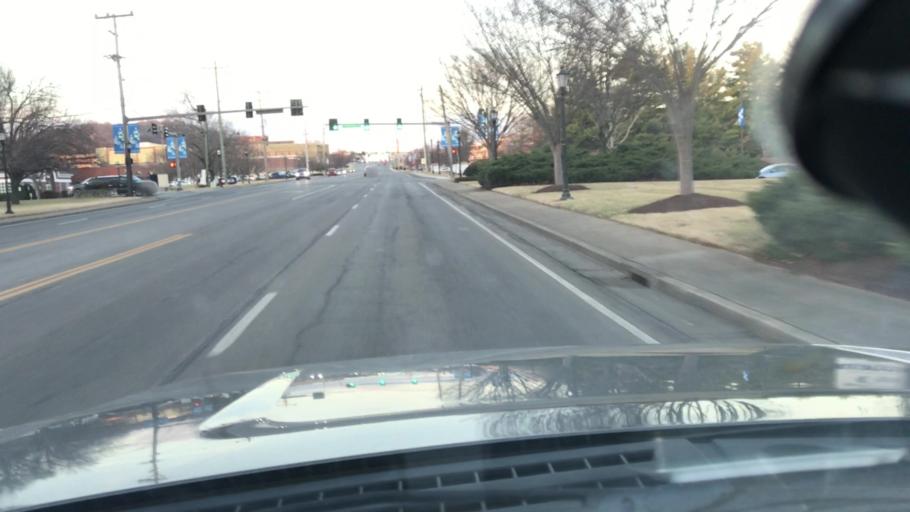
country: US
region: Tennessee
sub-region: Williamson County
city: Brentwood
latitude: 36.0278
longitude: -86.7917
